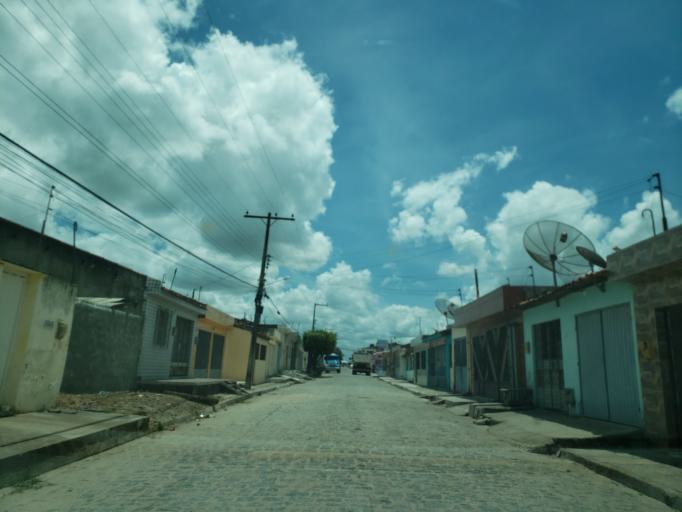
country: BR
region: Alagoas
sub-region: Uniao Dos Palmares
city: Uniao dos Palmares
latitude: -9.1631
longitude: -36.0220
